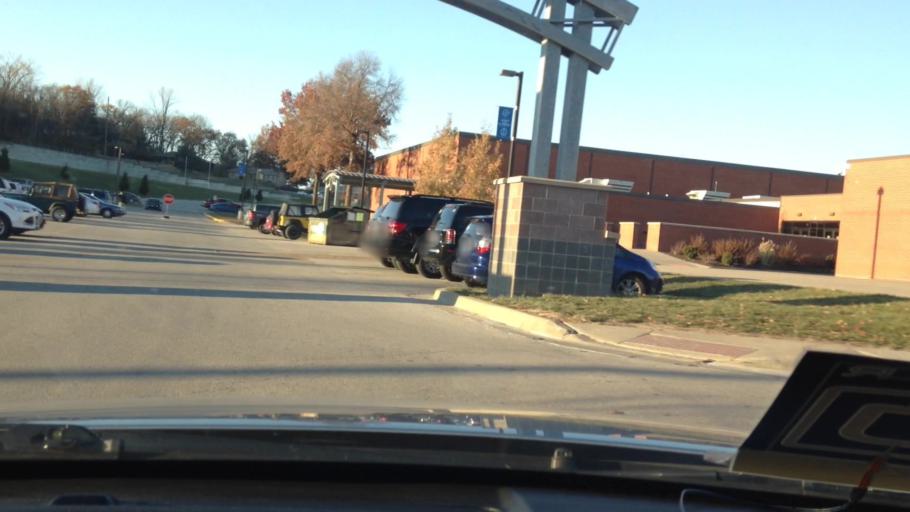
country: US
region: Kansas
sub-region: Leavenworth County
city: Leavenworth
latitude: 39.2954
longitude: -94.9300
